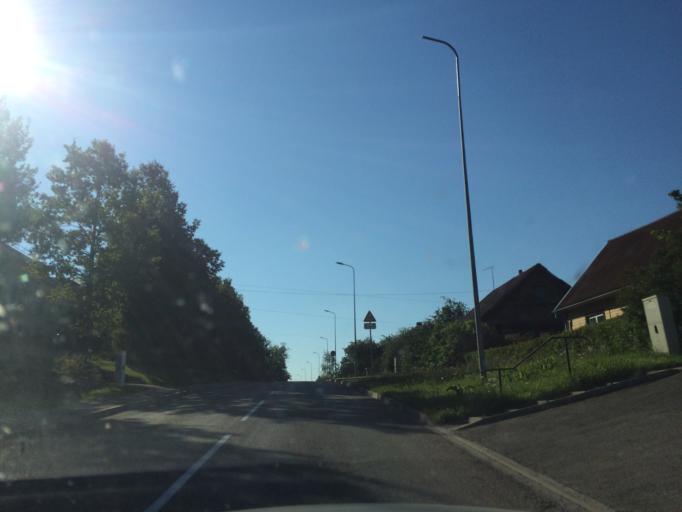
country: LV
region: Rezekne
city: Rezekne
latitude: 56.4954
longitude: 27.3229
